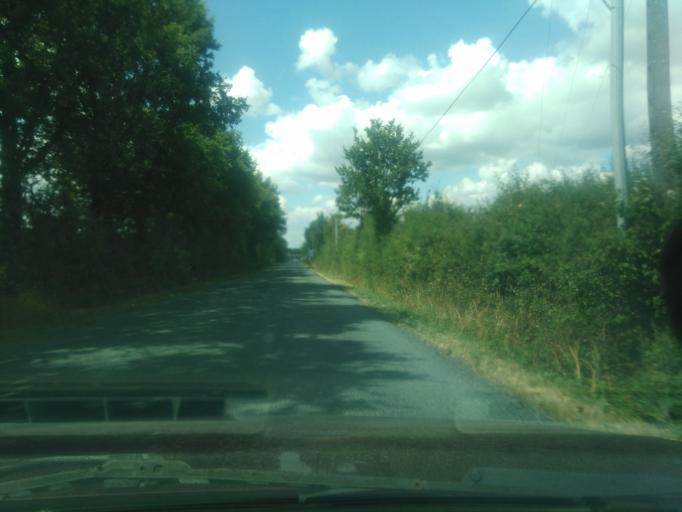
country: FR
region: Pays de la Loire
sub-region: Departement de la Vendee
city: Les Brouzils
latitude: 46.8711
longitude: -1.3184
